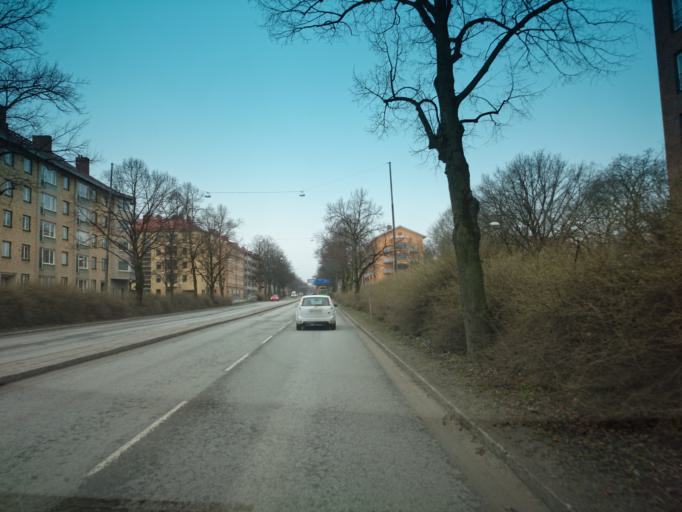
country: SE
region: Uppsala
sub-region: Uppsala Kommun
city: Uppsala
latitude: 59.8626
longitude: 17.6229
